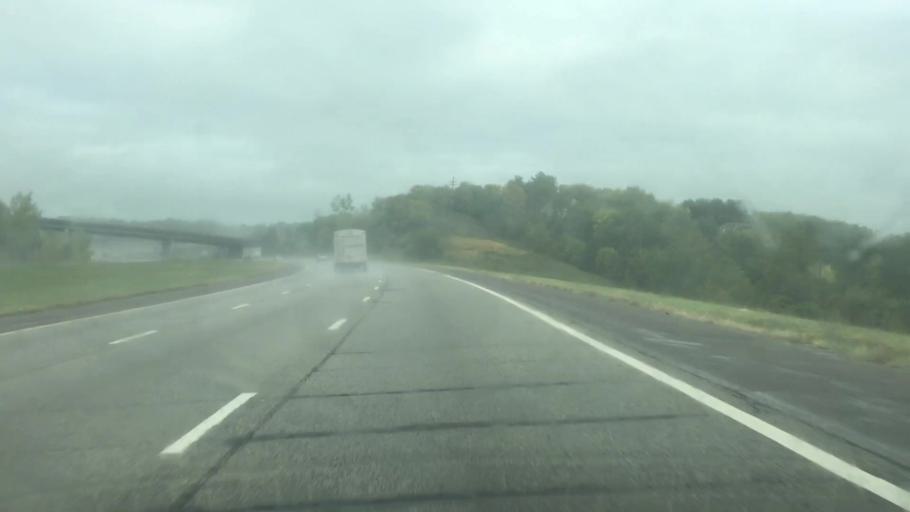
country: US
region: Kansas
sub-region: Johnson County
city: Lenexa
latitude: 38.9898
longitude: -94.7761
